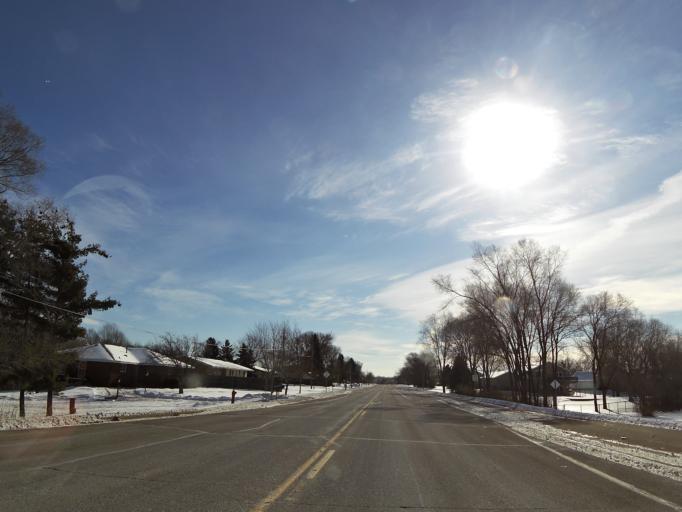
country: US
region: Minnesota
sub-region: Dakota County
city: Hastings
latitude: 44.7550
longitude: -92.8841
